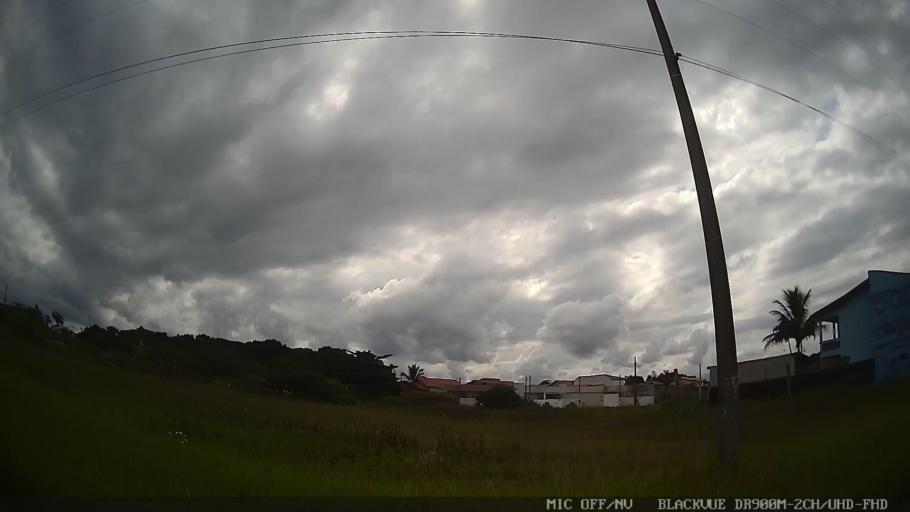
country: BR
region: Sao Paulo
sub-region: Itanhaem
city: Itanhaem
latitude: -24.2354
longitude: -46.8825
